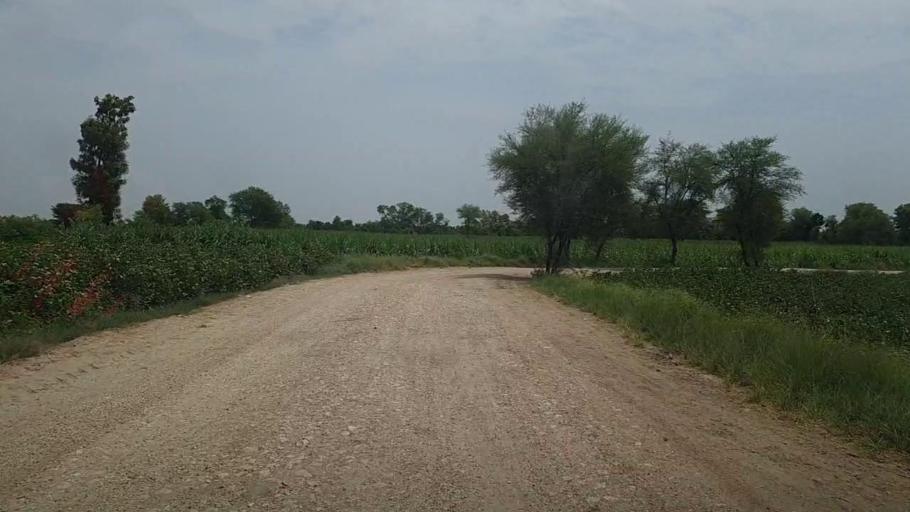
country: PK
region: Sindh
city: Karaundi
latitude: 26.9103
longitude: 68.3218
